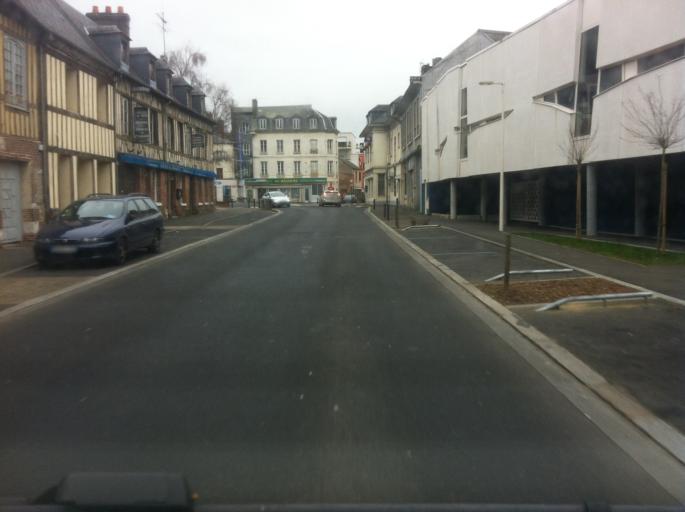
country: FR
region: Haute-Normandie
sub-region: Departement de l'Eure
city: Pont-Audemer
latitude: 49.3582
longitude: 0.5156
